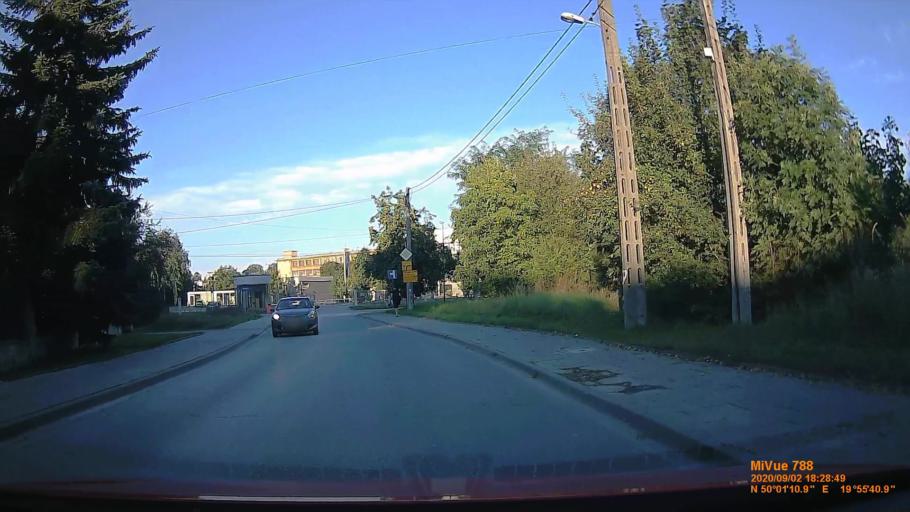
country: PL
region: Lesser Poland Voivodeship
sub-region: Krakow
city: Krakow
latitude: 50.0197
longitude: 19.9280
